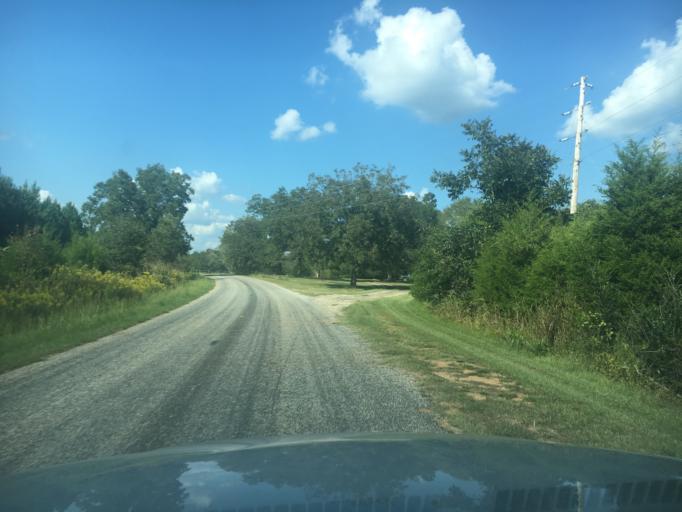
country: US
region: South Carolina
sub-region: Greenwood County
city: Ware Shoals
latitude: 34.4895
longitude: -82.2304
